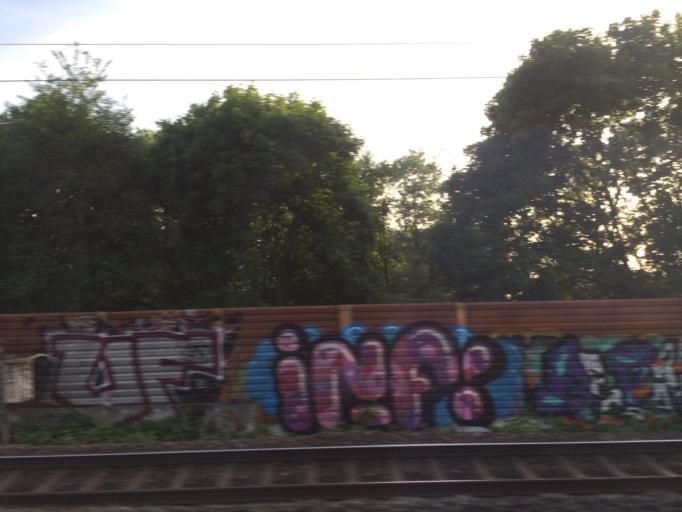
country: DE
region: Hesse
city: Niederrad
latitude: 50.0945
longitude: 8.6552
